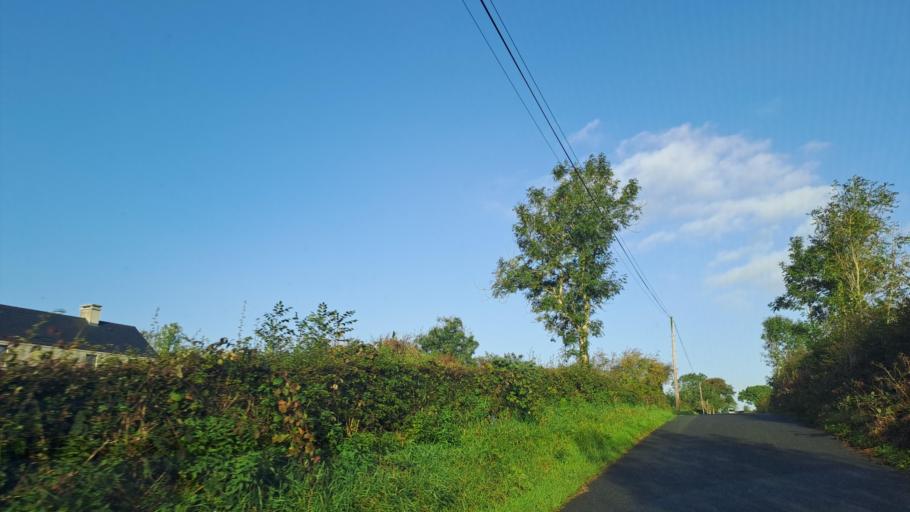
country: IE
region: Ulster
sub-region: County Monaghan
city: Castleblayney
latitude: 54.0616
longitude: -6.8211
